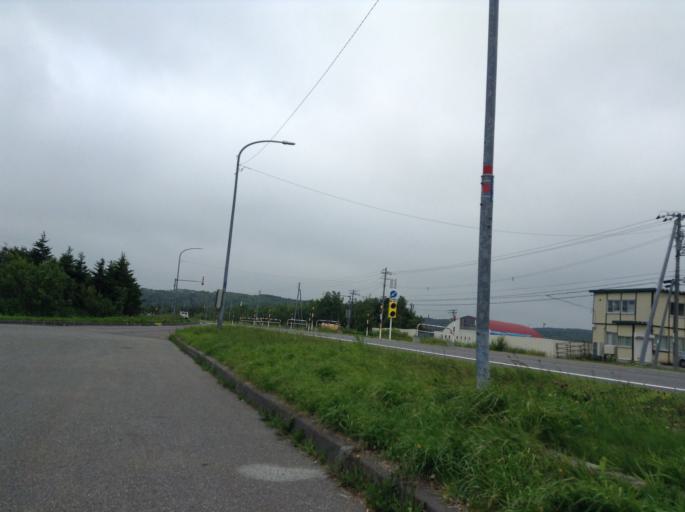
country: JP
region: Hokkaido
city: Wakkanai
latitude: 45.3637
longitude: 141.7295
